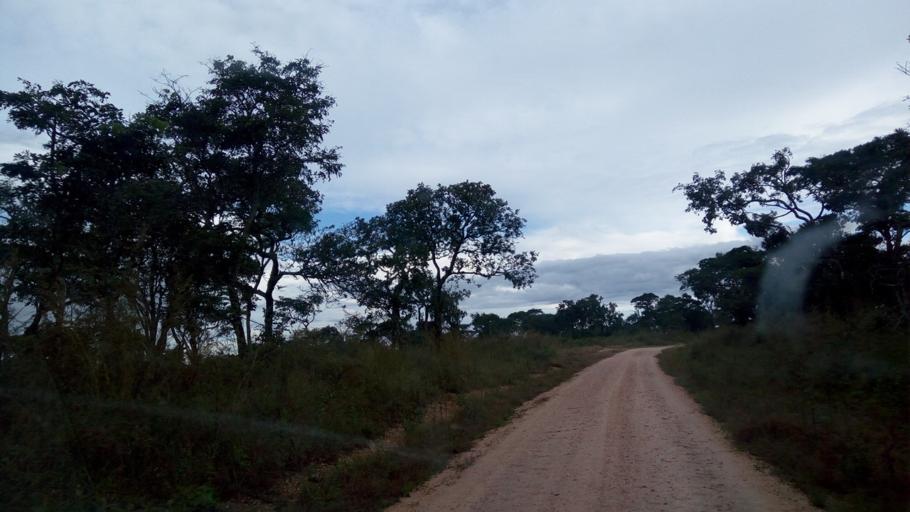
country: CD
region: Katanga
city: Kalemie
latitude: -6.6020
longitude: 29.0419
